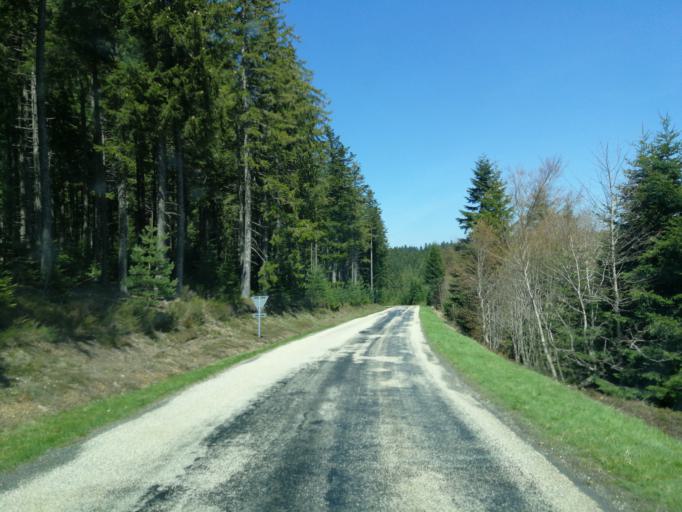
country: FR
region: Auvergne
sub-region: Departement de la Haute-Loire
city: Dunieres
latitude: 45.1356
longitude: 4.3959
